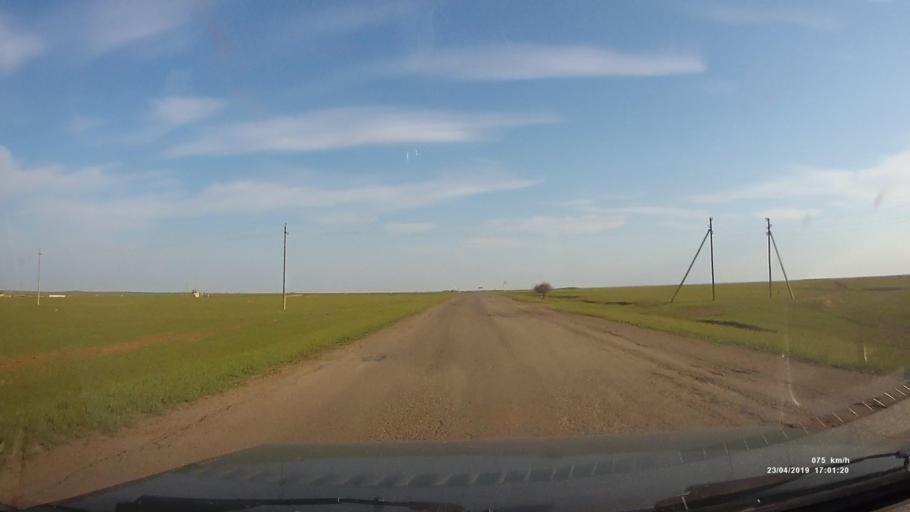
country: RU
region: Kalmykiya
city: Priyutnoye
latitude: 46.2973
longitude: 43.4077
